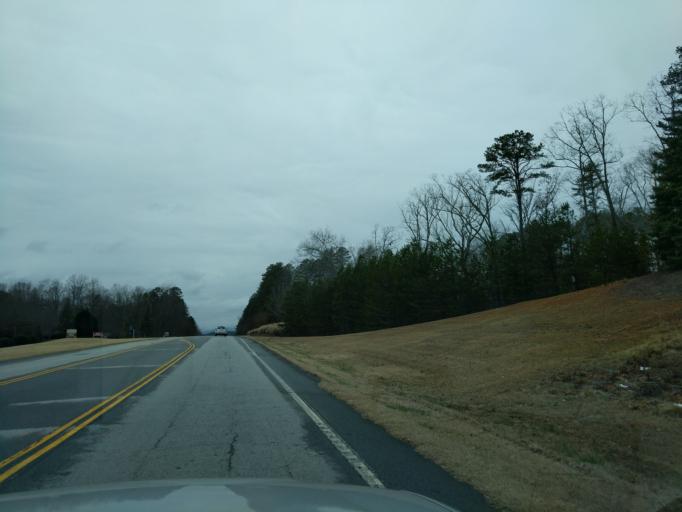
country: US
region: South Carolina
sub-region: Oconee County
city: Walhalla
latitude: 34.9139
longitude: -82.9219
